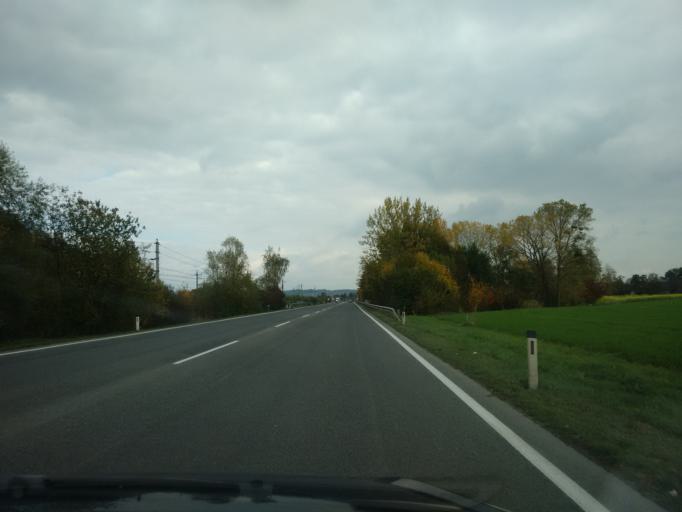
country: AT
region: Upper Austria
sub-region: Politischer Bezirk Vocklabruck
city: Redlham
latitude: 48.0353
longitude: 13.7427
